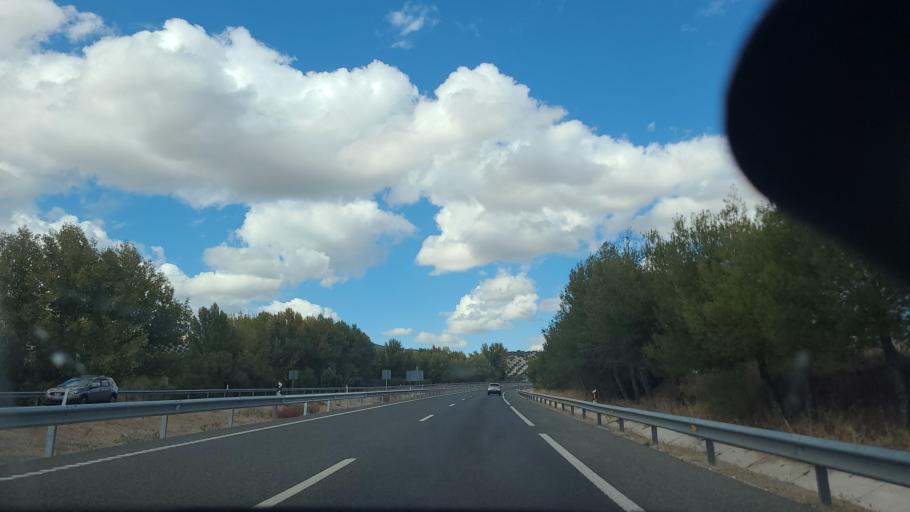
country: ES
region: Andalusia
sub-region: Provincia de Jaen
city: Noalejo
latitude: 37.5134
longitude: -3.6365
